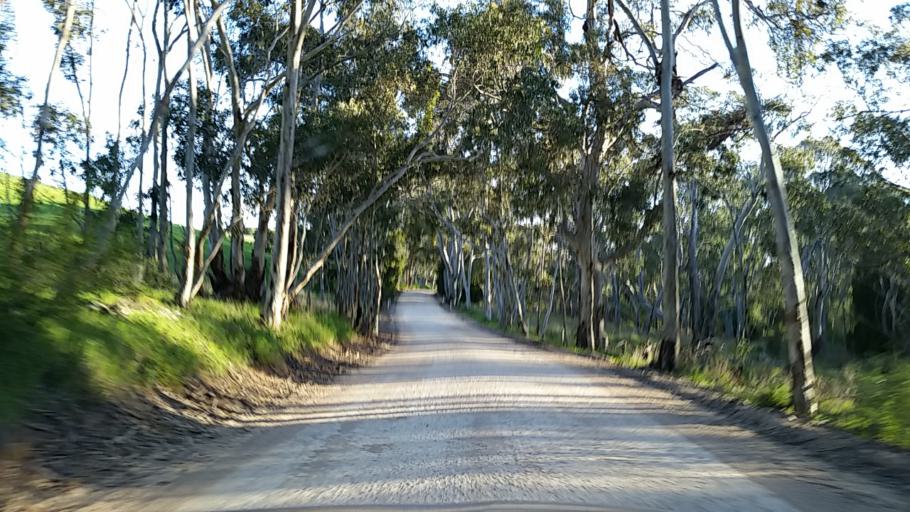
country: AU
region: South Australia
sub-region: Alexandrina
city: Mount Compass
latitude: -35.2763
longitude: 138.7012
